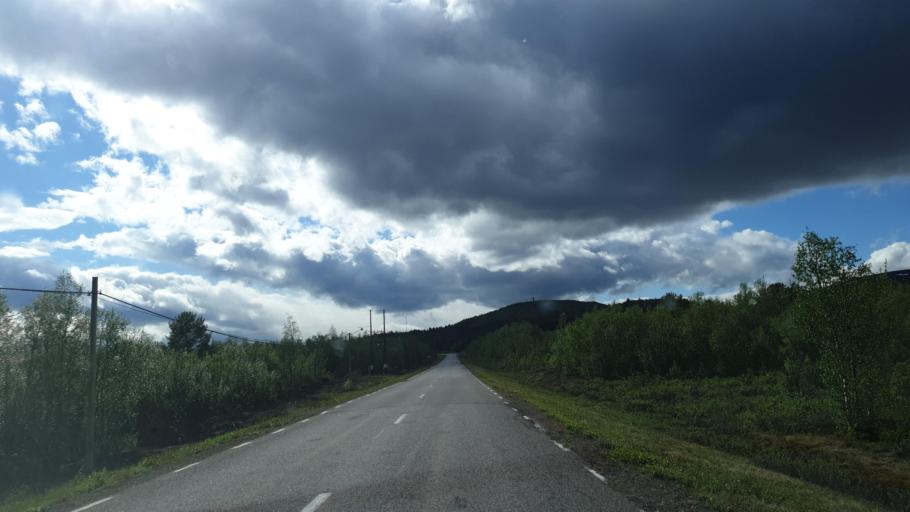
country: SE
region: Norrbotten
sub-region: Kiruna Kommun
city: Kiruna
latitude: 67.8687
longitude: 19.3687
